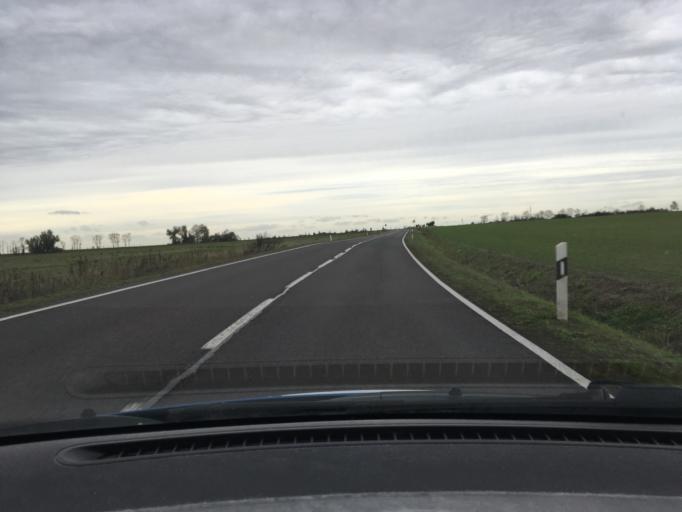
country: DE
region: Saxony-Anhalt
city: Leitzkau
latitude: 52.0399
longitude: 11.9774
